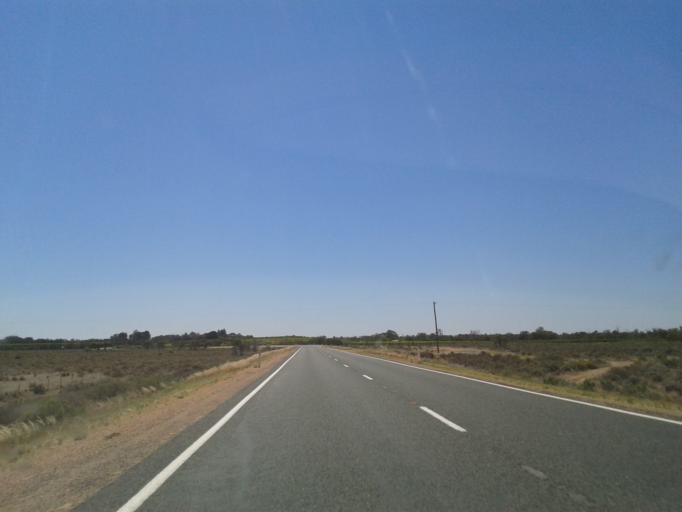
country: AU
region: New South Wales
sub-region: Wentworth
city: Dareton
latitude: -34.1026
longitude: 142.0007
